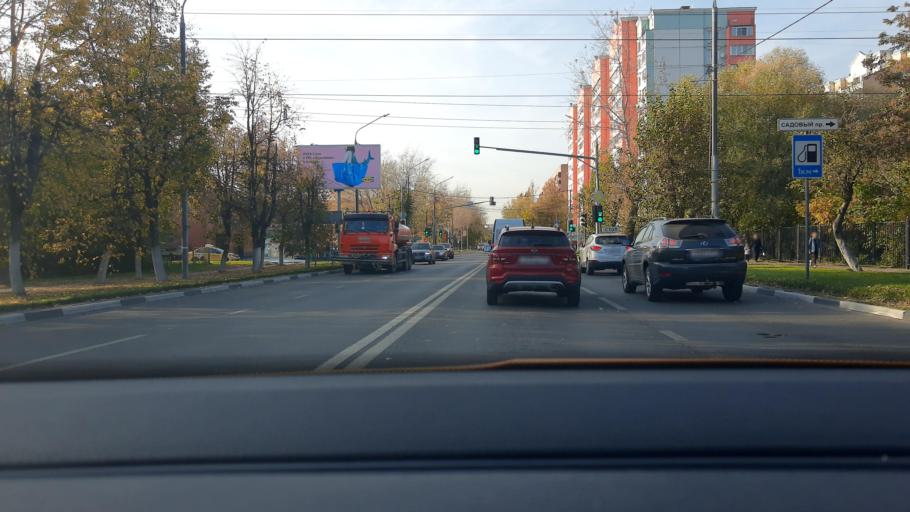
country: RU
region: Moskovskaya
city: Reutov
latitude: 55.7657
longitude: 37.8508
